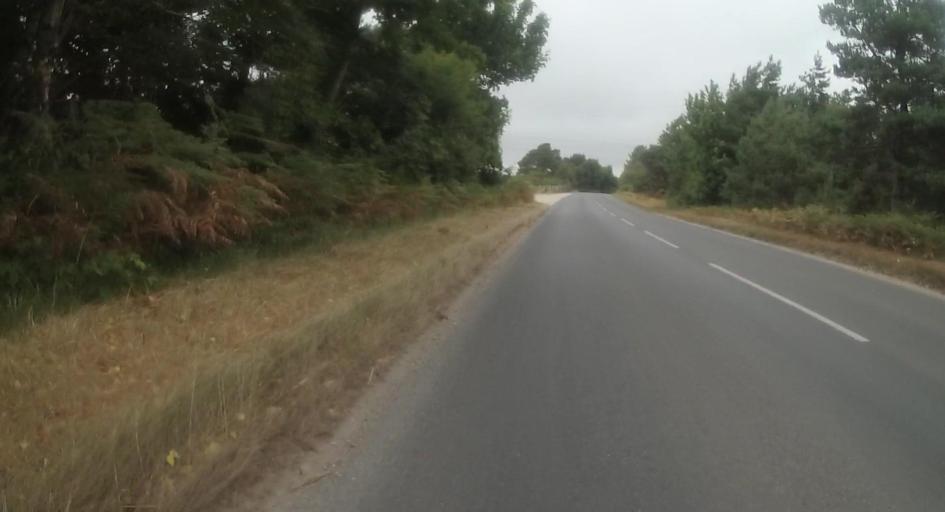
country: GB
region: England
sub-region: Dorset
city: Wool
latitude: 50.7015
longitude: -2.1960
